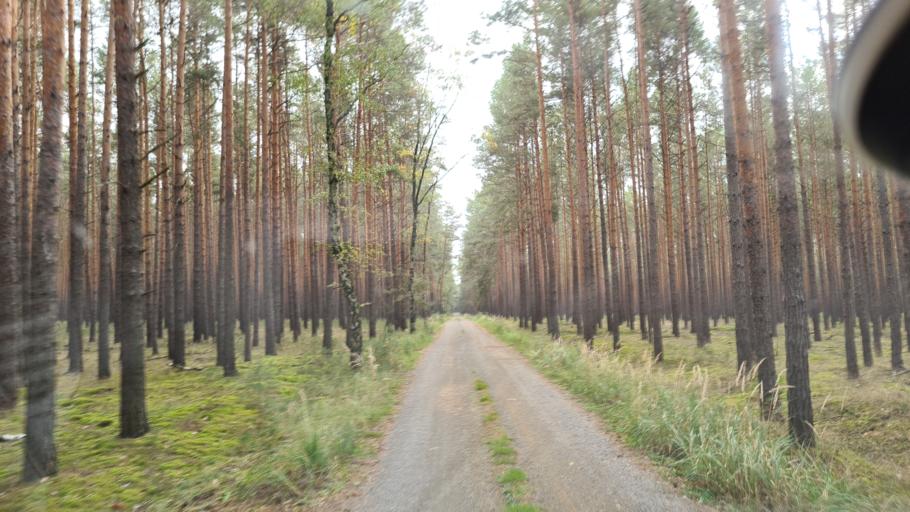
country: DE
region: Brandenburg
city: Schonewalde
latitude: 51.7142
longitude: 13.5766
